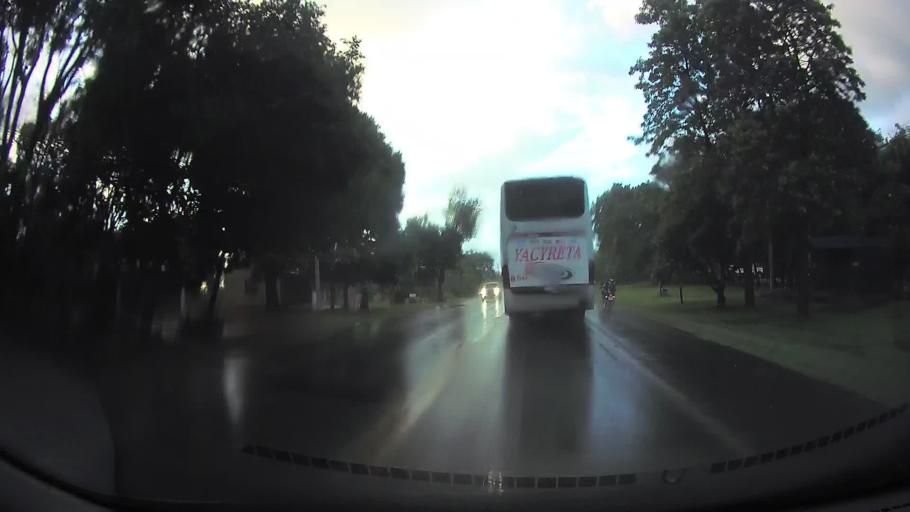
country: PY
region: Paraguari
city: Yaguaron
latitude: -25.5853
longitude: -57.2420
